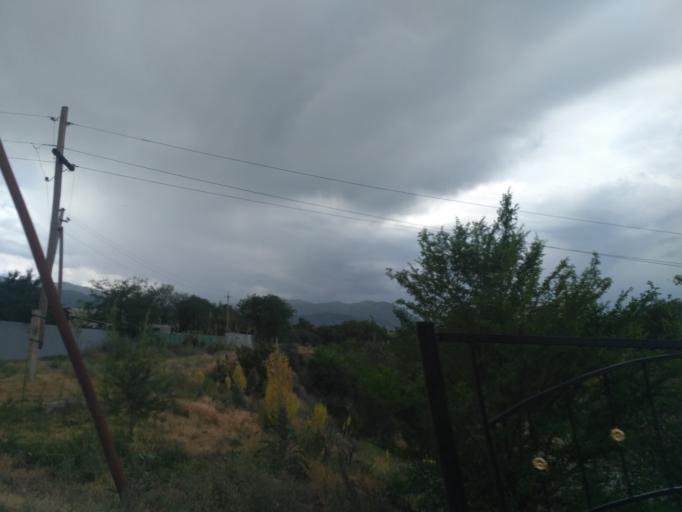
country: KZ
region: Almaty Oblysy
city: Burunday
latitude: 43.2083
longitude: 76.6357
